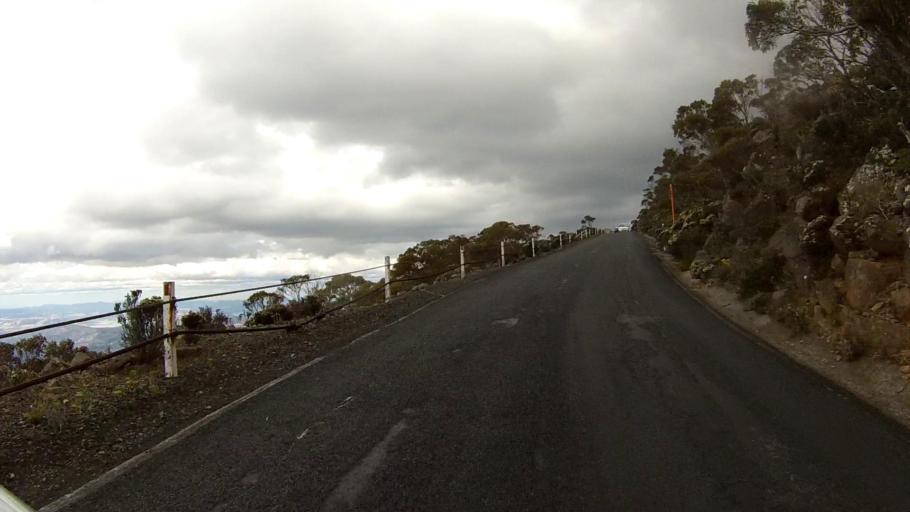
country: AU
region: Tasmania
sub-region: Glenorchy
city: West Moonah
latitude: -42.8915
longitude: 147.2297
